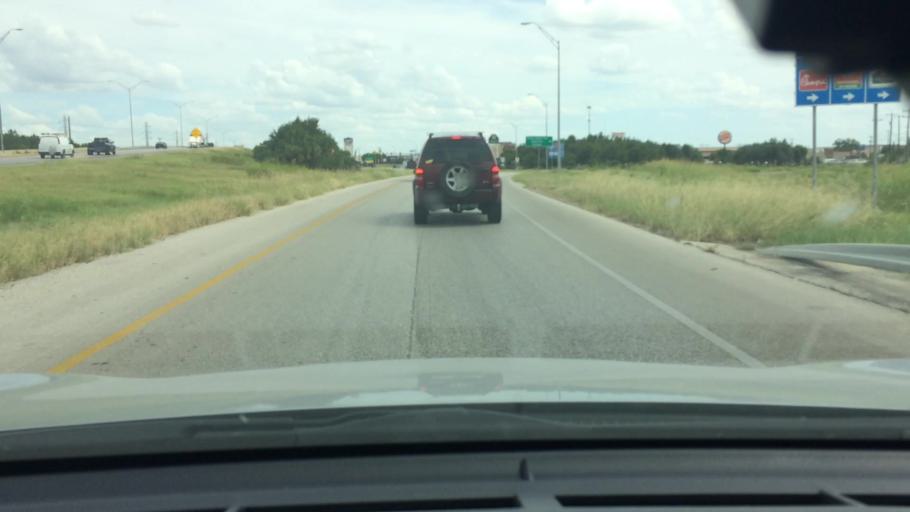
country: US
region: Texas
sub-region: Bexar County
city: China Grove
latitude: 29.3552
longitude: -98.4300
